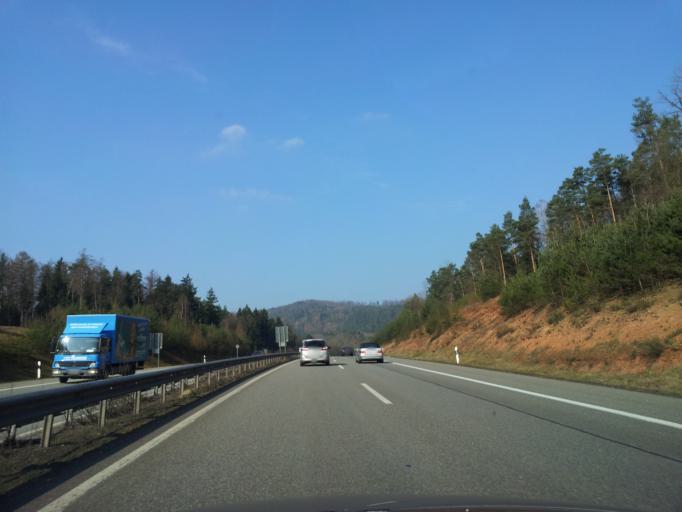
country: DE
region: Rheinland-Pfalz
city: Ruppertsweiler
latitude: 49.1969
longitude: 7.7052
